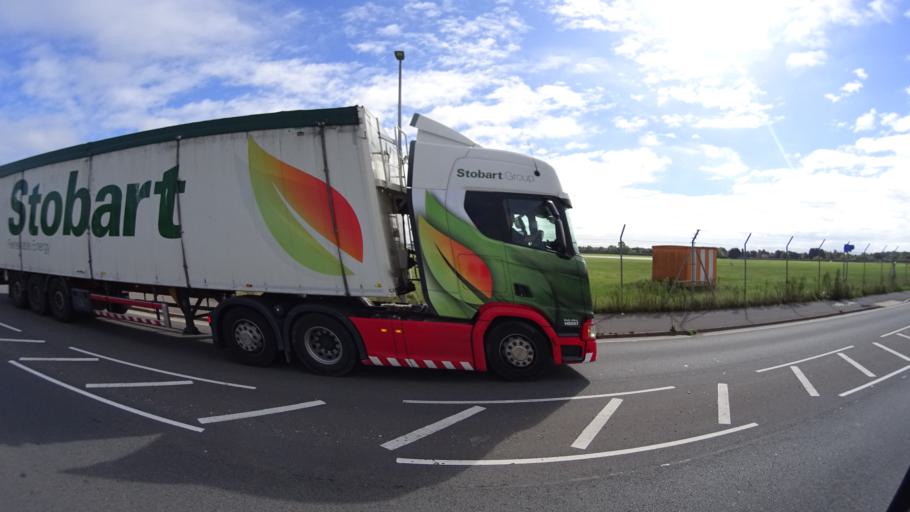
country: GB
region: England
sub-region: Dorset
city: Ferndown
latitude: 50.7783
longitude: -1.8601
